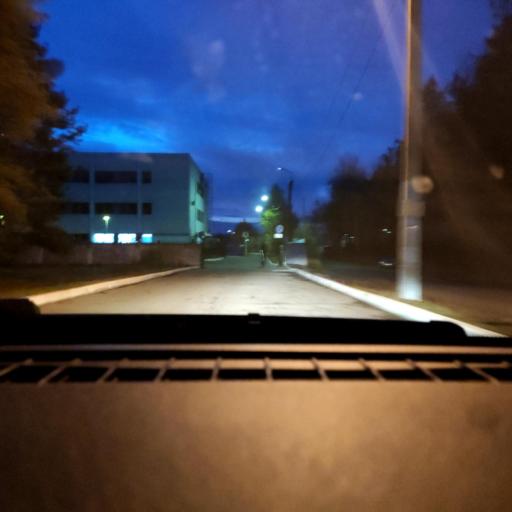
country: RU
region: Voronezj
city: Somovo
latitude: 51.7409
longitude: 39.2988
